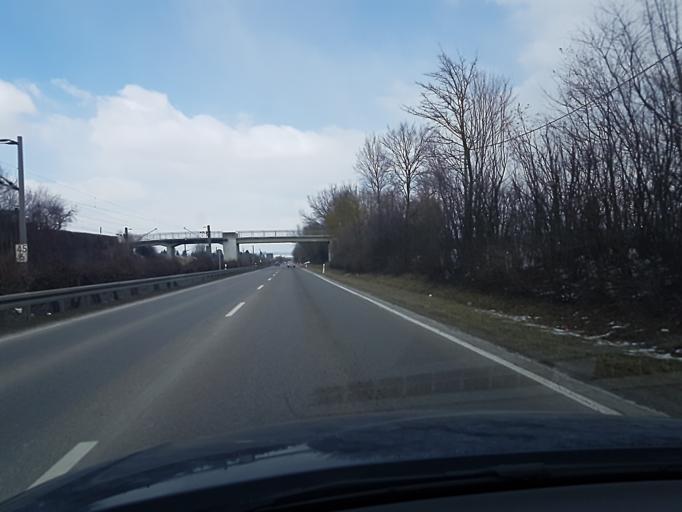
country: DE
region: Baden-Wuerttemberg
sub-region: Regierungsbezirk Stuttgart
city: Herrenberg
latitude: 48.5643
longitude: 8.8538
